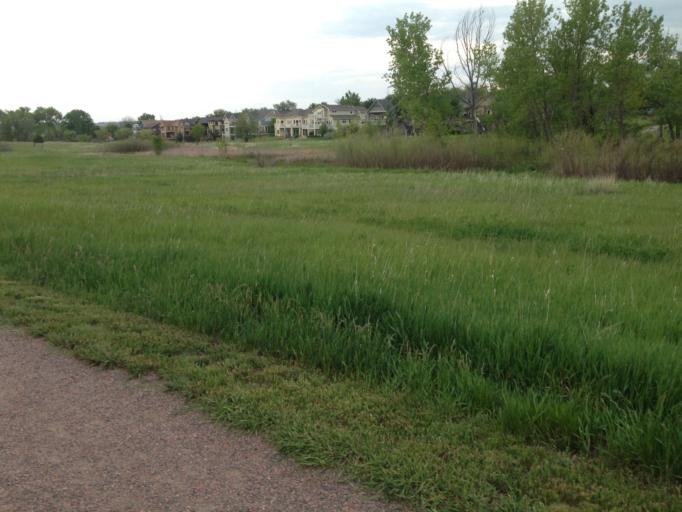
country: US
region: Colorado
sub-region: Boulder County
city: Lafayette
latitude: 40.0036
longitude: -105.0890
